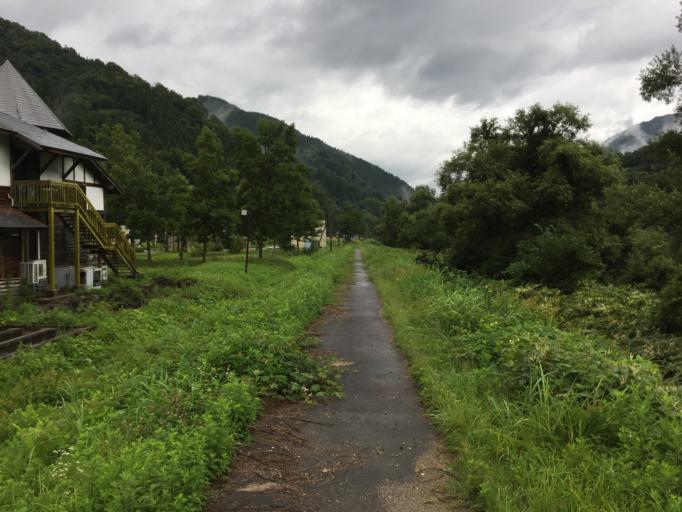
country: JP
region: Toyama
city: Yatsuomachi-higashikumisaka
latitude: 36.4572
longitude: 137.0424
